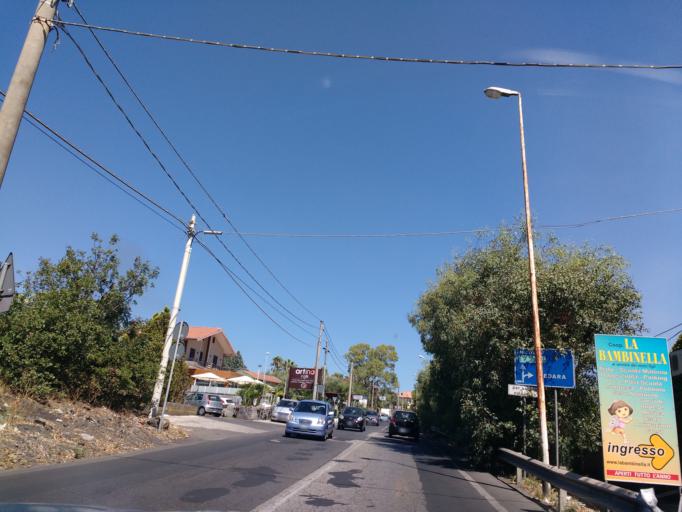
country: IT
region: Sicily
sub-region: Catania
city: Mascalucia
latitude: 37.5864
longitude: 15.0495
